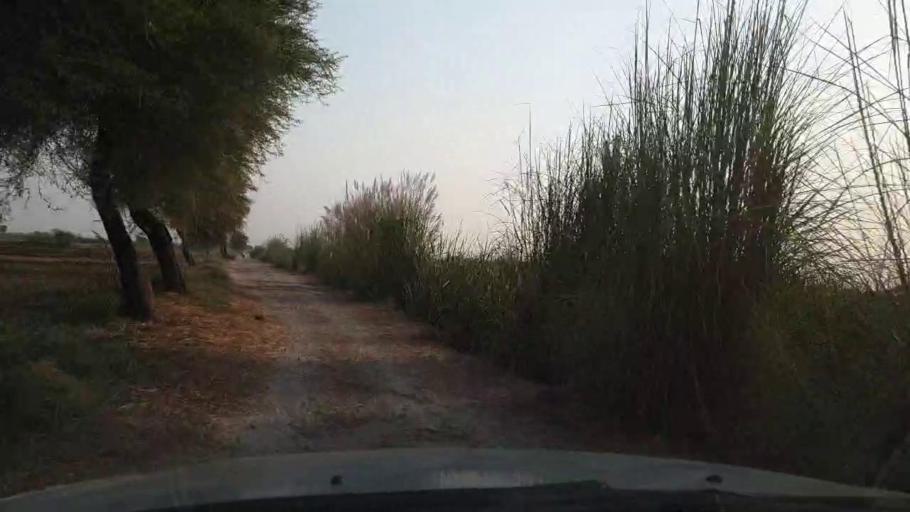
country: PK
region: Sindh
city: Tando Muhammad Khan
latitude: 25.0245
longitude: 68.4388
